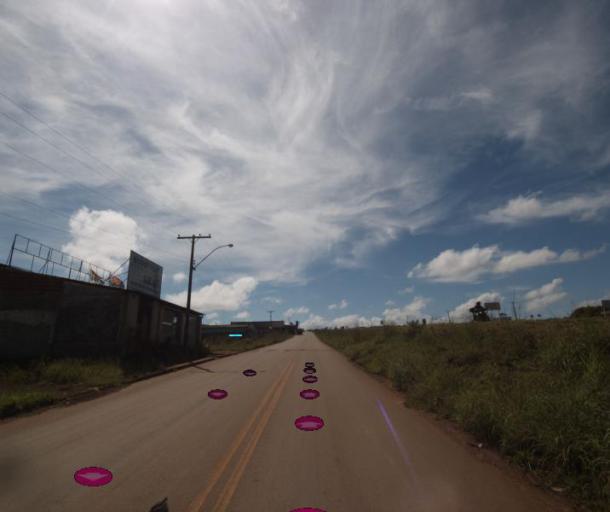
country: BR
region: Federal District
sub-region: Brasilia
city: Brasilia
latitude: -15.7393
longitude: -48.3048
